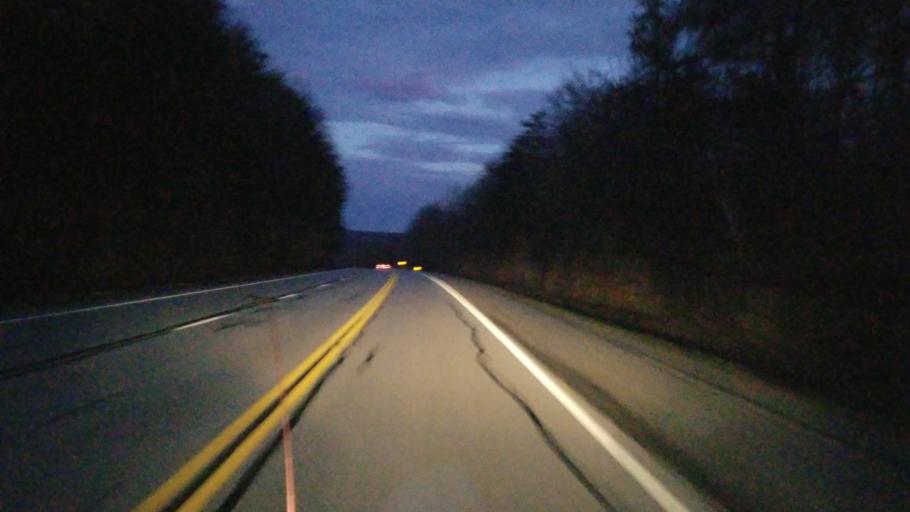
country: US
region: Tennessee
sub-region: Sequatchie County
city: Dunlap
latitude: 35.4847
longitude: -85.4661
